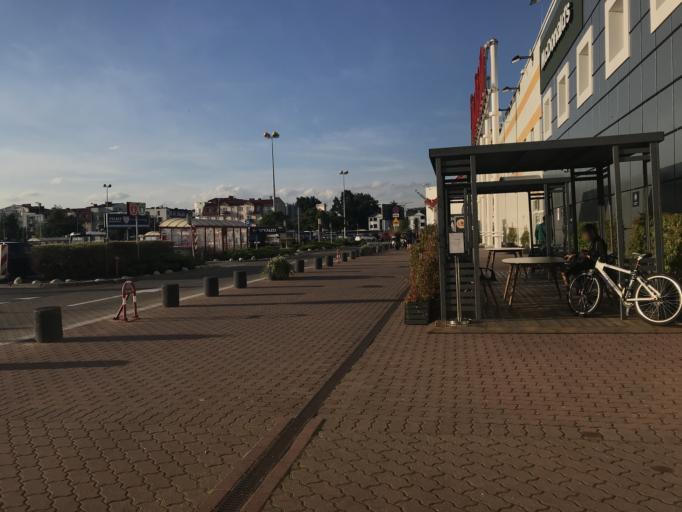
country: PL
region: Masovian Voivodeship
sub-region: Warszawa
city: Ursynow
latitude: 52.1412
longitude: 21.0260
